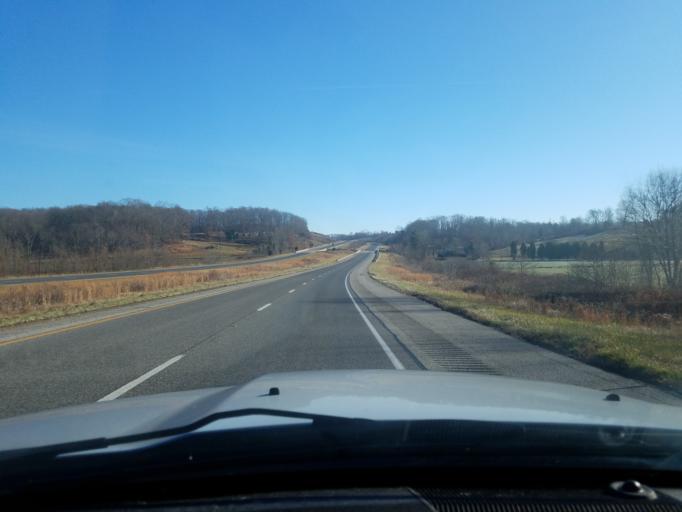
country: US
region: Indiana
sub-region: Dubois County
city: Ferdinand
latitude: 38.2159
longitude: -86.7384
